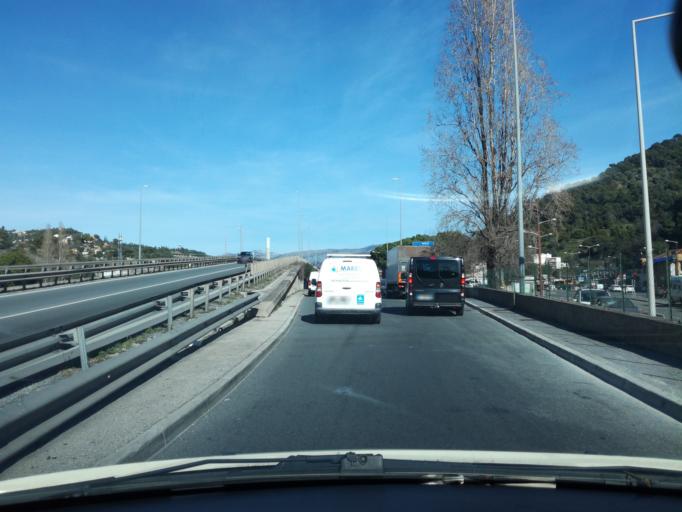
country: FR
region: Provence-Alpes-Cote d'Azur
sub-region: Departement des Alpes-Maritimes
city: Saint-Andre-de-la-Roche
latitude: 43.7306
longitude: 7.2846
